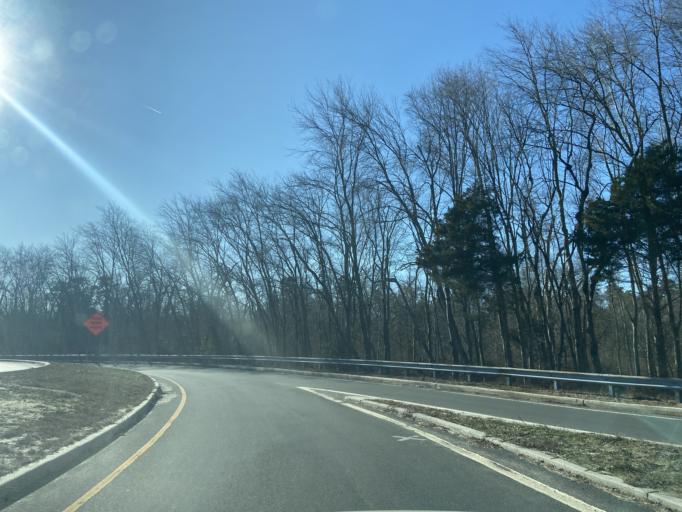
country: US
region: New Jersey
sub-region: Gloucester County
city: Newfield
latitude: 39.5215
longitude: -75.0708
